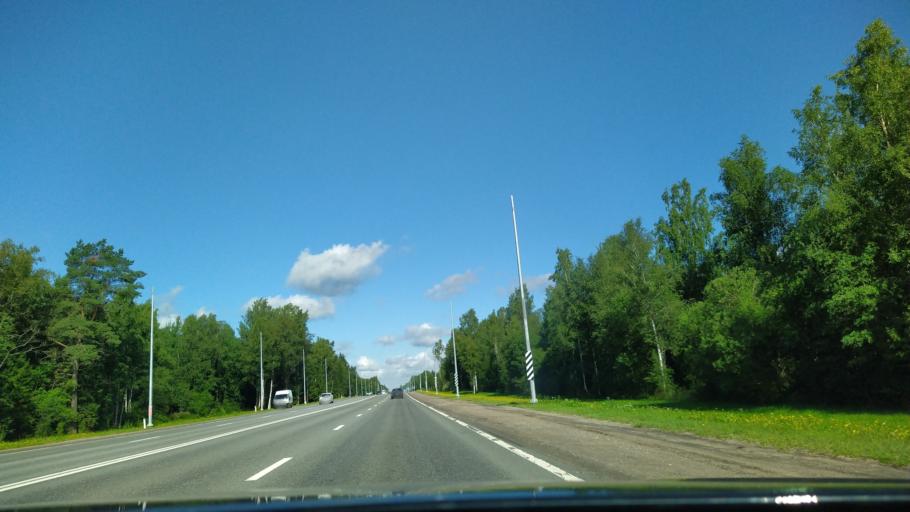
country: RU
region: Leningrad
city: Tosno
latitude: 59.5746
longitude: 30.8160
